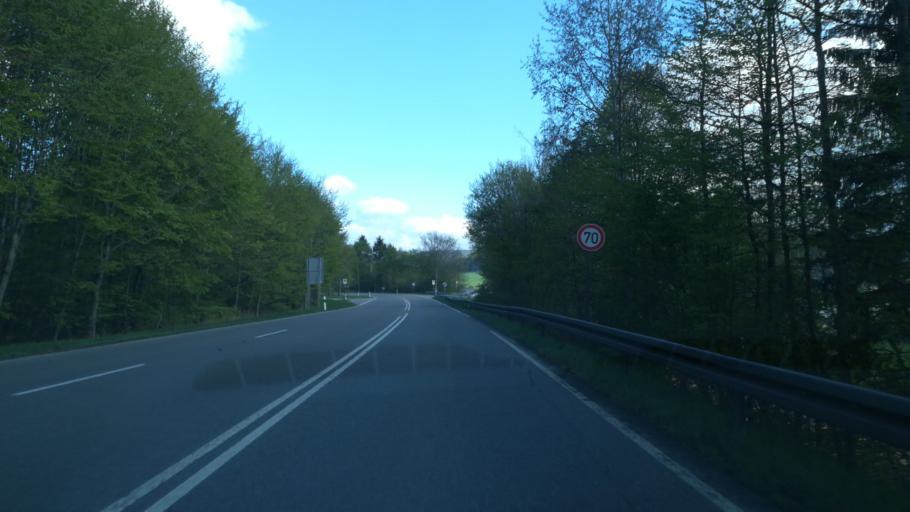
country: DE
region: Baden-Wuerttemberg
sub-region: Freiburg Region
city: Blumberg
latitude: 47.8333
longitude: 8.5637
